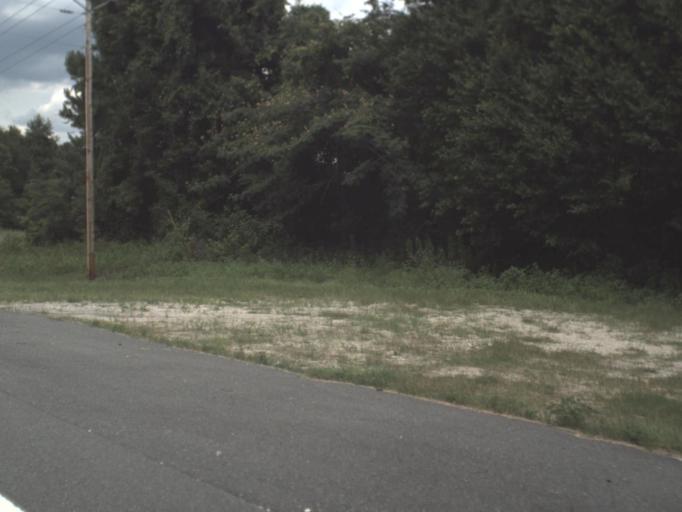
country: US
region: Florida
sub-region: Alachua County
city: Alachua
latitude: 29.8662
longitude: -82.3426
